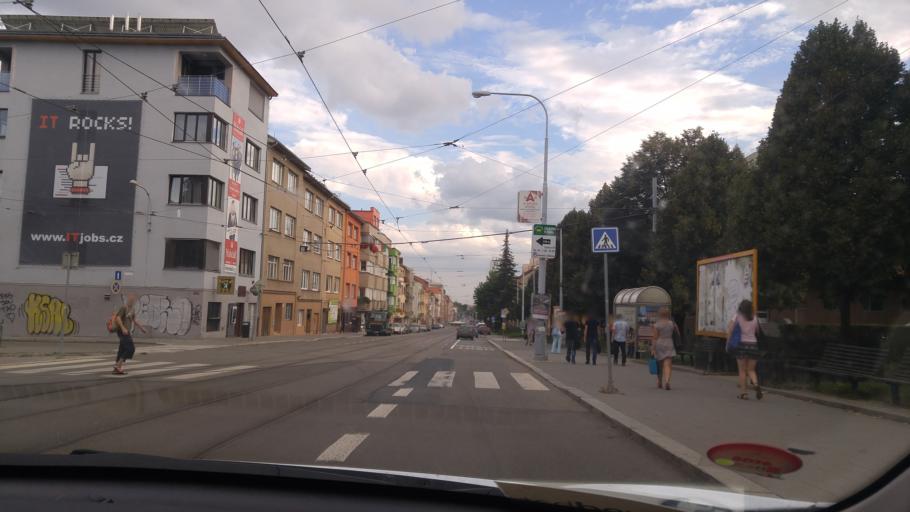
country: CZ
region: South Moravian
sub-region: Mesto Brno
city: Mokra Hora
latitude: 49.2252
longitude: 16.5827
